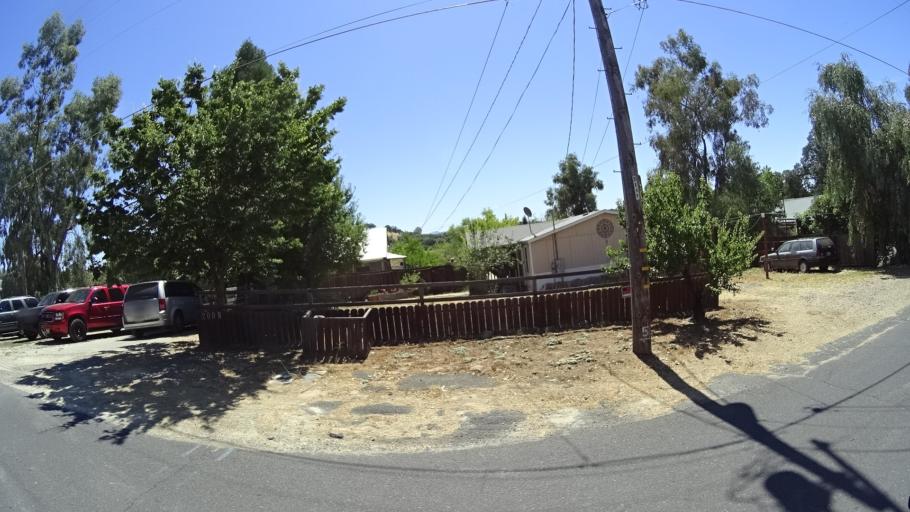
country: US
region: California
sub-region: Calaveras County
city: Angels Camp
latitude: 38.0851
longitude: -120.5572
